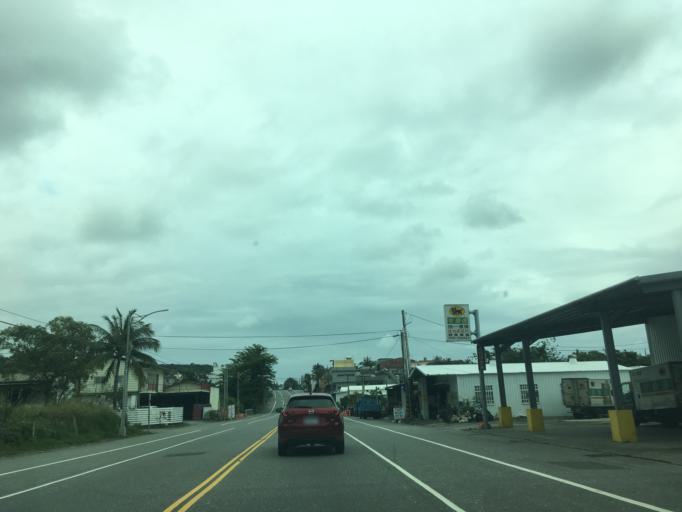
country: TW
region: Taiwan
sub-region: Taitung
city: Taitung
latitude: 23.1089
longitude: 121.3835
